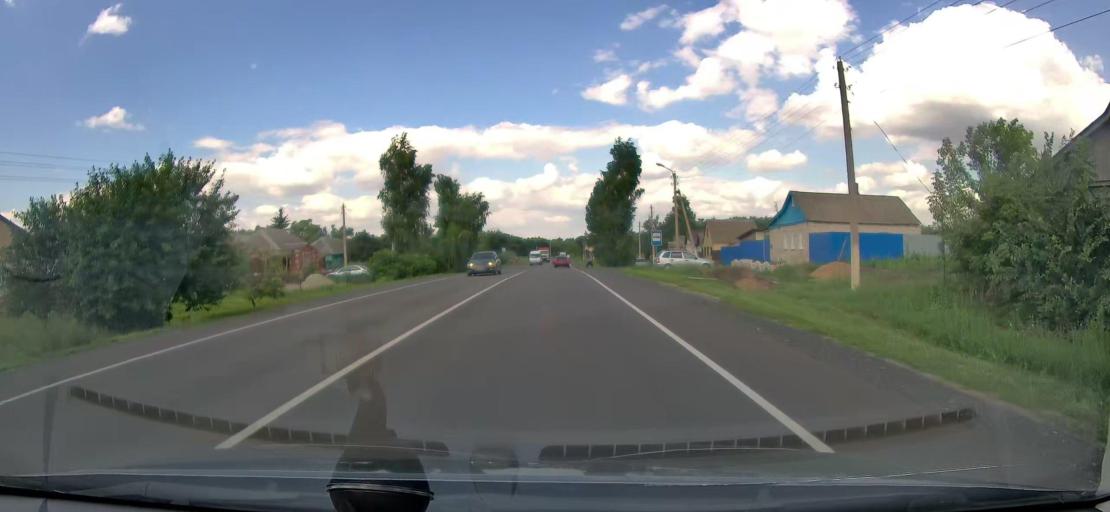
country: RU
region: Kursk
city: Zolotukhino
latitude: 51.9212
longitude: 36.3069
